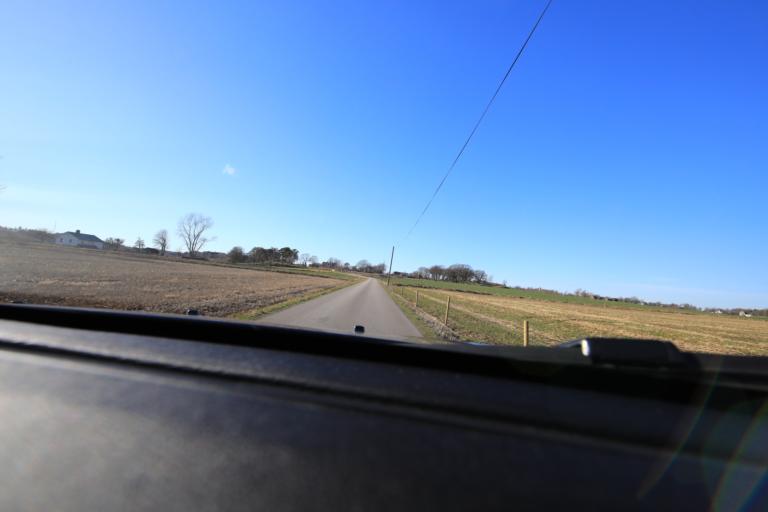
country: SE
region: Halland
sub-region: Varbergs Kommun
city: Tvaaker
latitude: 57.0662
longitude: 12.3862
